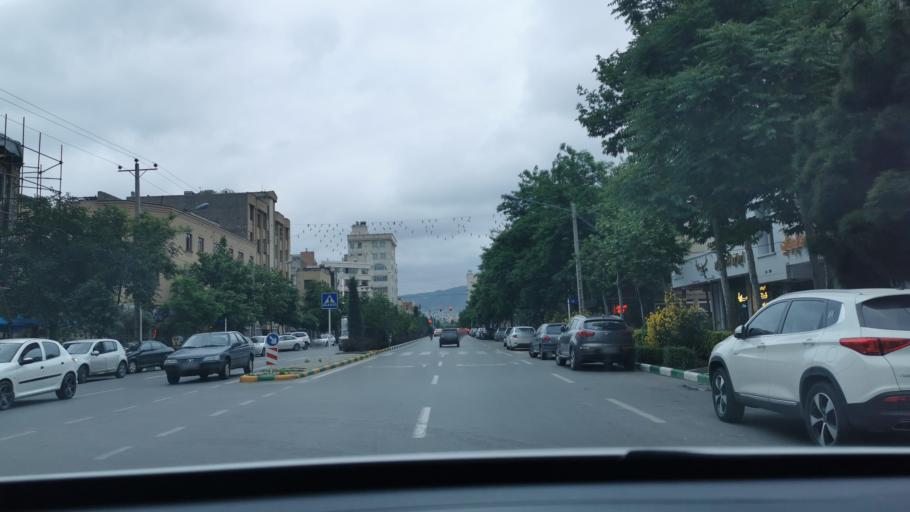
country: IR
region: Razavi Khorasan
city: Mashhad
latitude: 36.3259
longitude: 59.5272
